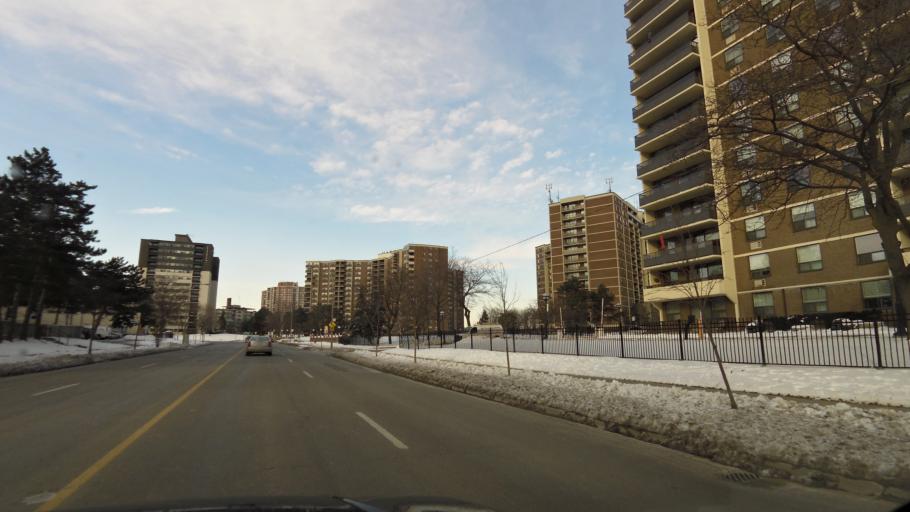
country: CA
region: Ontario
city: Etobicoke
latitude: 43.6505
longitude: -79.5691
